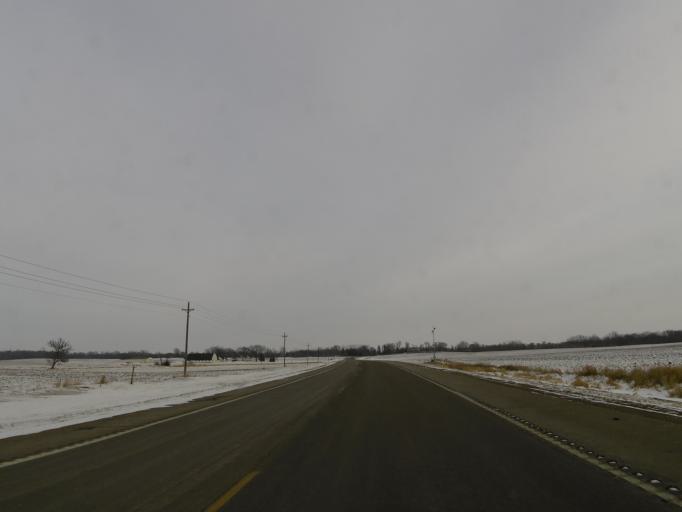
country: US
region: Minnesota
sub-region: McLeod County
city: Lester Prairie
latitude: 44.9061
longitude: -93.9884
